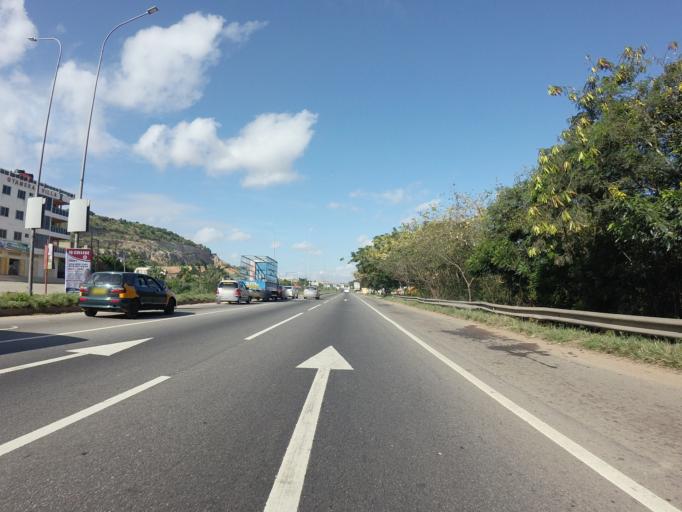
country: GH
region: Central
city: Kasoa
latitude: 5.5519
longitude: -0.3670
